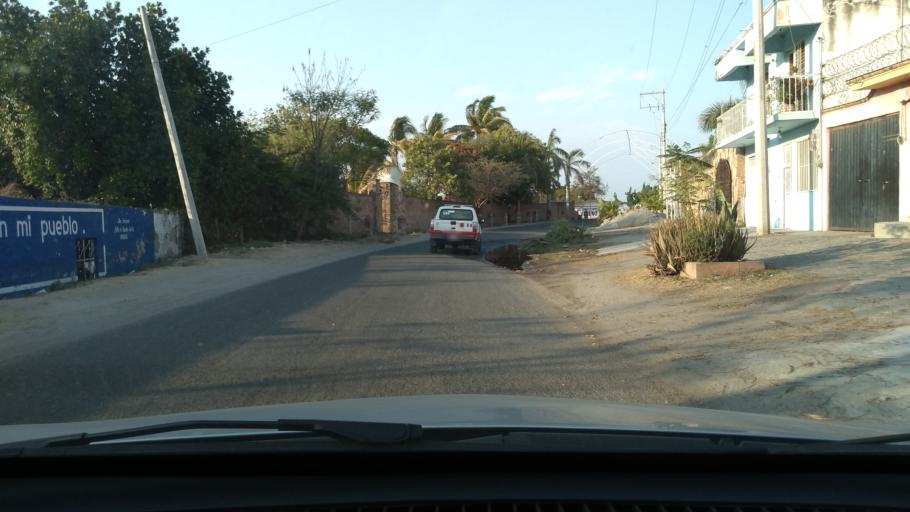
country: MX
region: Morelos
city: Puente de Ixtla
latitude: 18.6097
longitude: -99.3174
